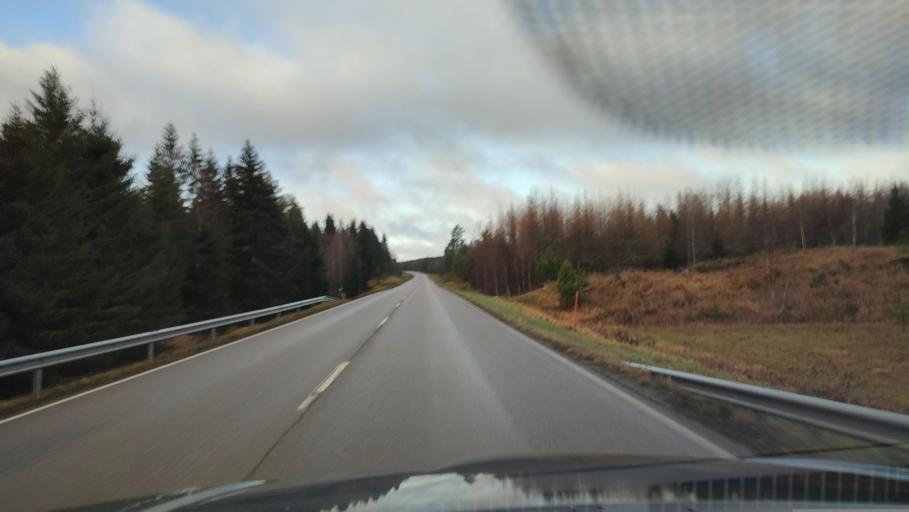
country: FI
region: Ostrobothnia
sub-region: Sydosterbotten
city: Kristinestad
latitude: 62.3025
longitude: 21.4259
